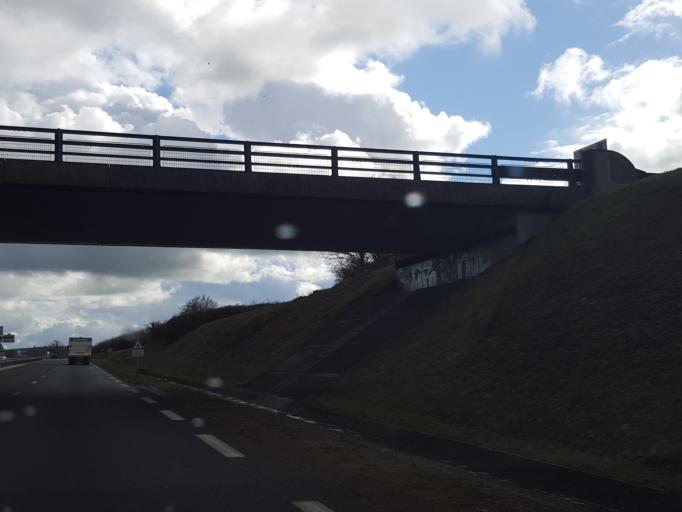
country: FR
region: Pays de la Loire
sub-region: Departement de la Vendee
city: La Ferriere
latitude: 46.6719
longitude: -1.3609
